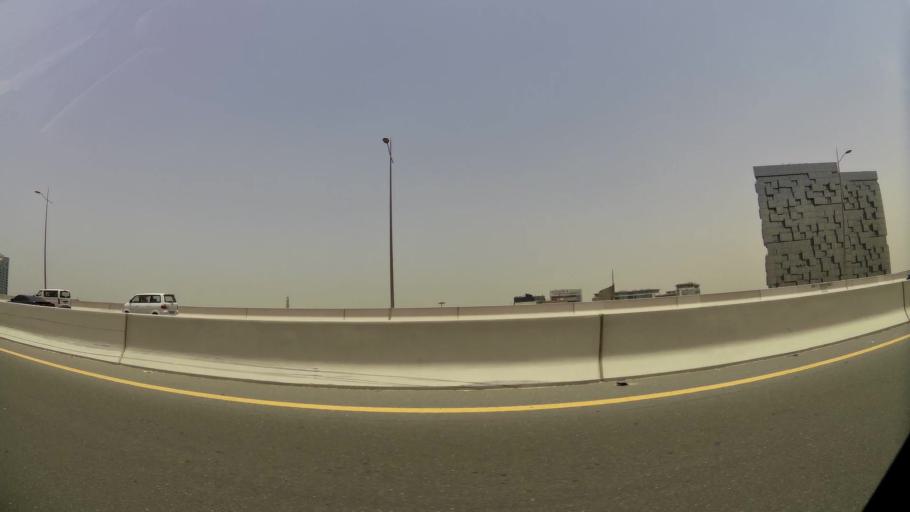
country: AE
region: Ash Shariqah
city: Sharjah
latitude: 25.2287
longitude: 55.3528
